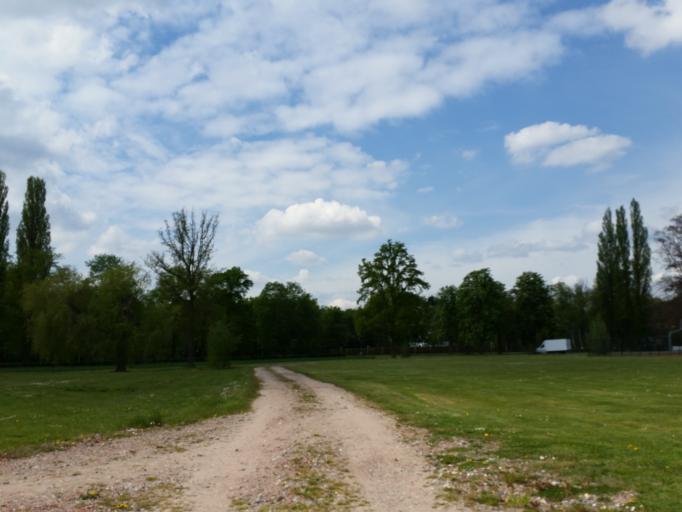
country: BE
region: Flanders
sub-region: Provincie Vlaams-Brabant
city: Zemst
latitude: 50.9814
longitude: 4.5075
